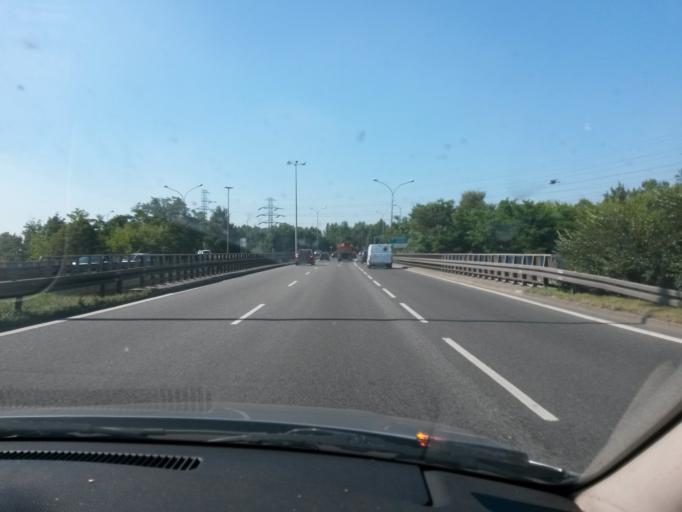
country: PL
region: Silesian Voivodeship
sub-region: Katowice
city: Katowice
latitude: 50.2601
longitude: 19.0473
